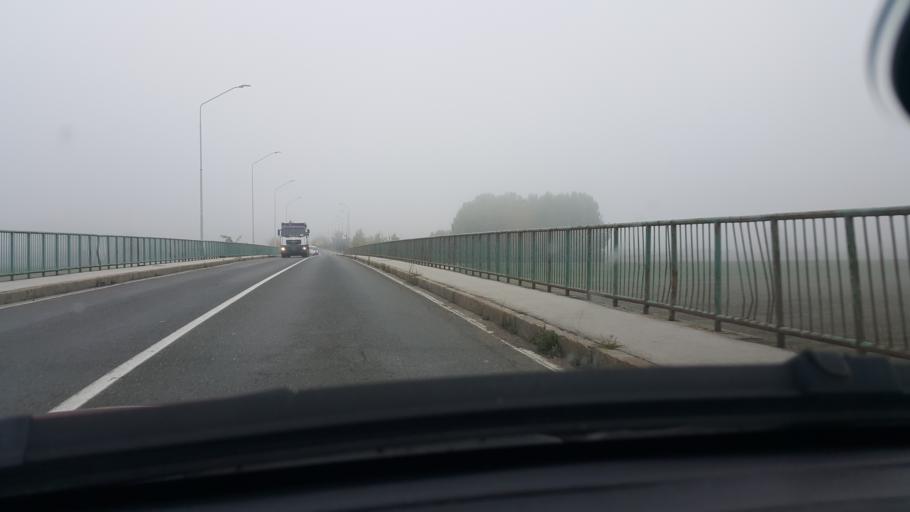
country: SI
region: Brezice
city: Brezice
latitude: 45.8945
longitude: 15.6034
